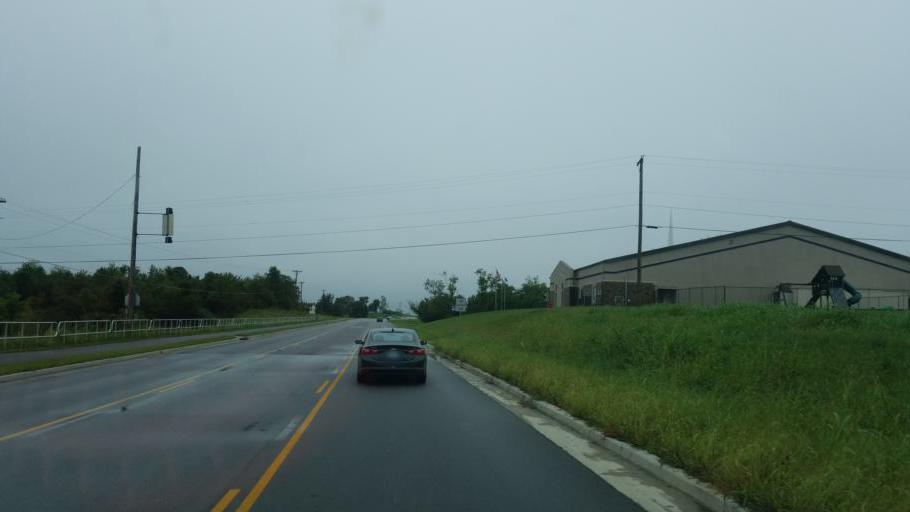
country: US
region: Ohio
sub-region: Brown County
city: Aberdeen
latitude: 38.6321
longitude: -83.7825
